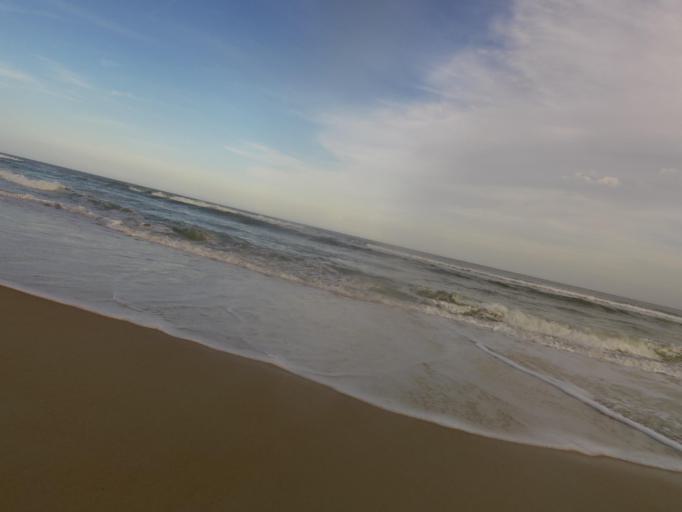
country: US
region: Florida
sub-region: Flagler County
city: Palm Coast
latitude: 29.6223
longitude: -81.1927
